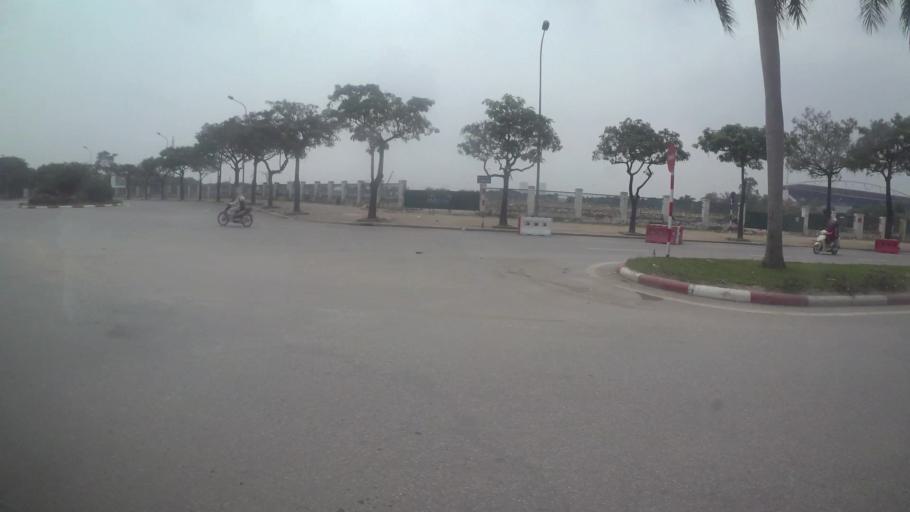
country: VN
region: Ha Noi
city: Cau Dien
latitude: 21.0179
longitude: 105.7665
